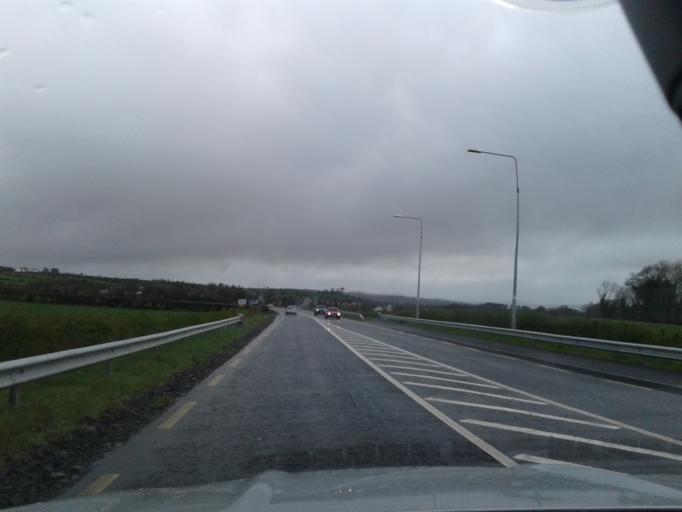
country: IE
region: Ulster
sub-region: County Donegal
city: Letterkenny
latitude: 54.9788
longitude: -7.6779
